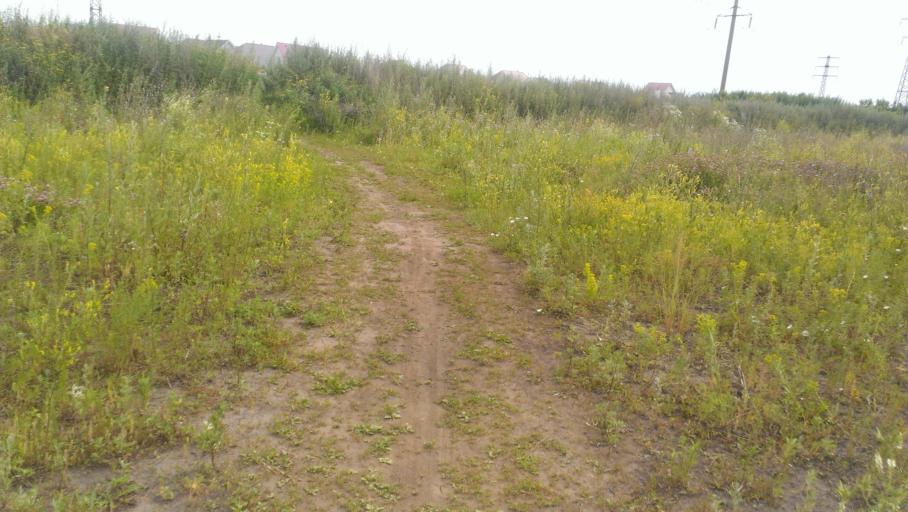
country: RU
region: Altai Krai
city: Novosilikatnyy
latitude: 53.3718
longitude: 83.6482
